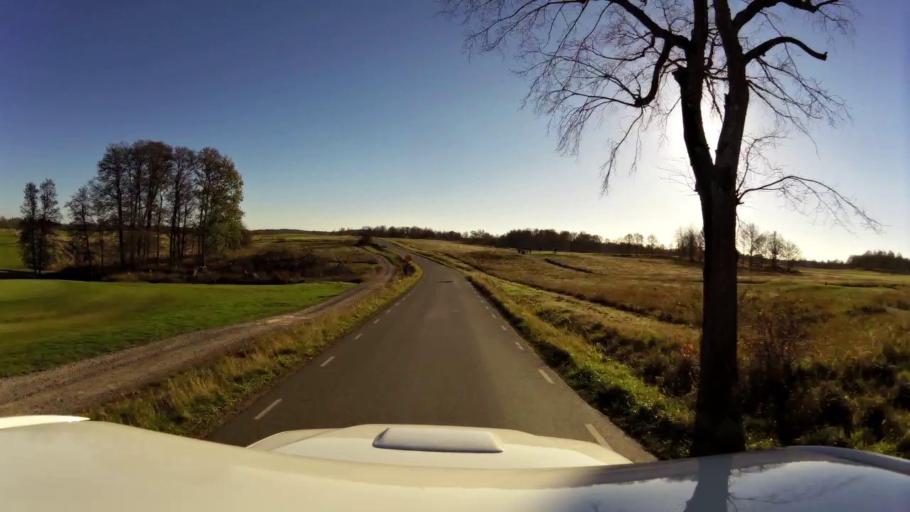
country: SE
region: OEstergoetland
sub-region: Kinda Kommun
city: Rimforsa
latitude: 58.2430
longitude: 15.6706
